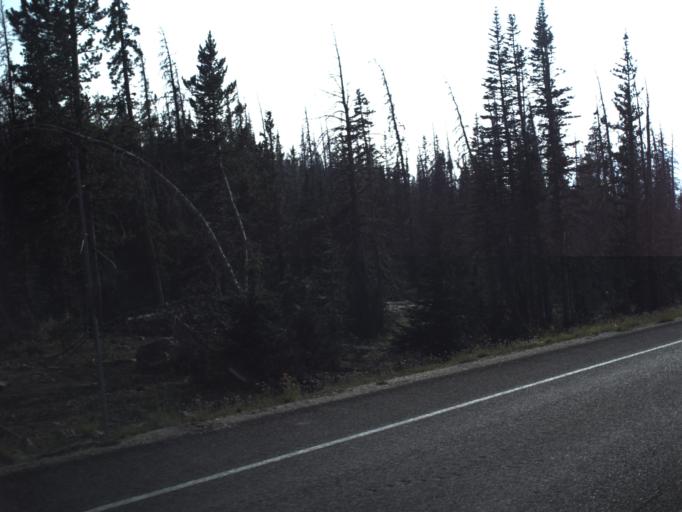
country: US
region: Utah
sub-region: Summit County
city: Kamas
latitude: 40.6813
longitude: -110.9204
